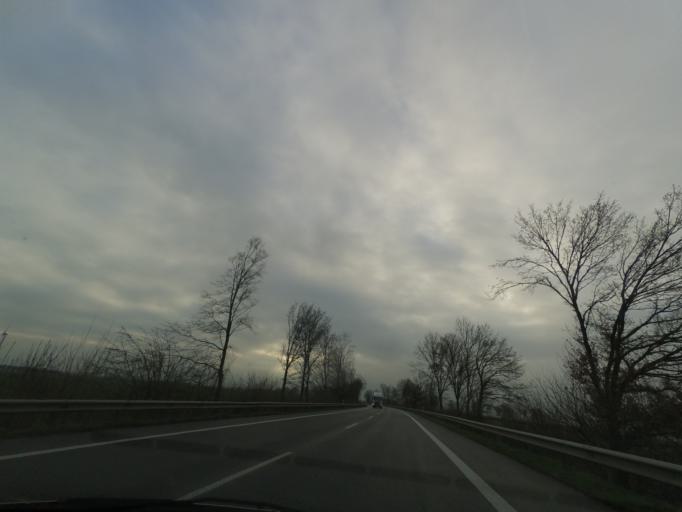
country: DE
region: North Rhine-Westphalia
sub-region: Regierungsbezirk Dusseldorf
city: Neubrueck
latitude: 51.1555
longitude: 6.5933
